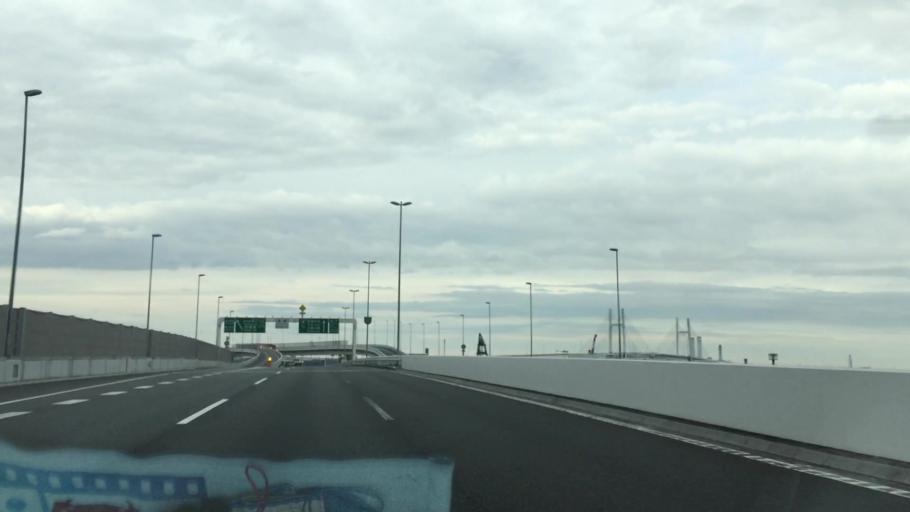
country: JP
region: Kanagawa
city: Yokohama
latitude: 35.4321
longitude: 139.6713
